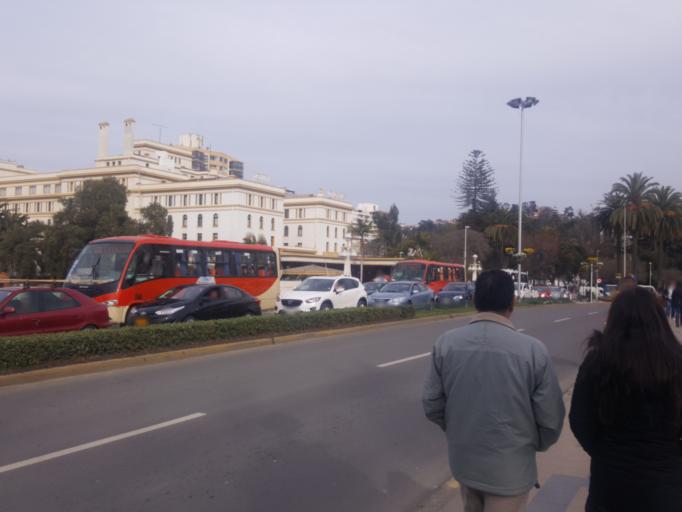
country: CL
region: Valparaiso
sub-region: Provincia de Valparaiso
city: Vina del Mar
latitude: -33.0228
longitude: -71.5516
